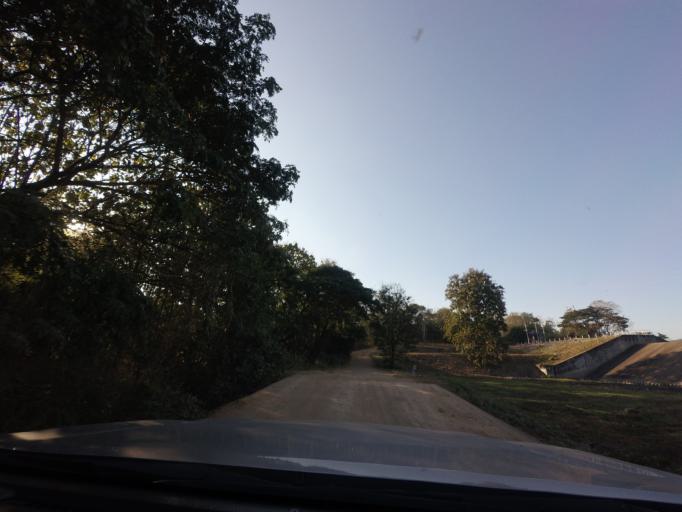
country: TH
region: Lampang
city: Mae Mo
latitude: 18.4125
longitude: 99.7460
